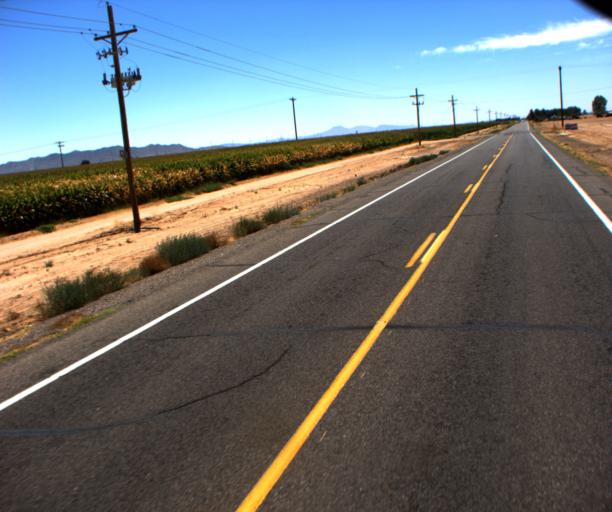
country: US
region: Arizona
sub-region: Pinal County
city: Arizona City
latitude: 32.8797
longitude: -111.6174
